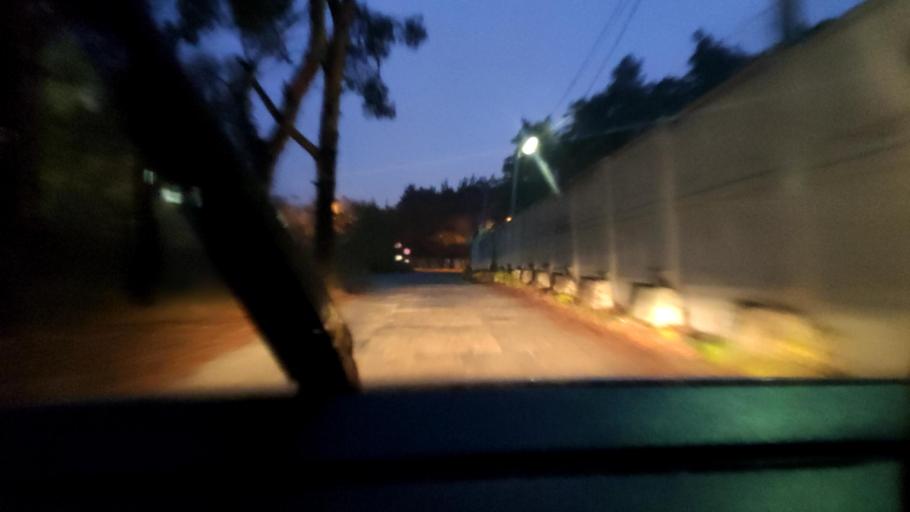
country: RU
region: Voronezj
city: Podgornoye
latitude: 51.6883
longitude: 39.1392
